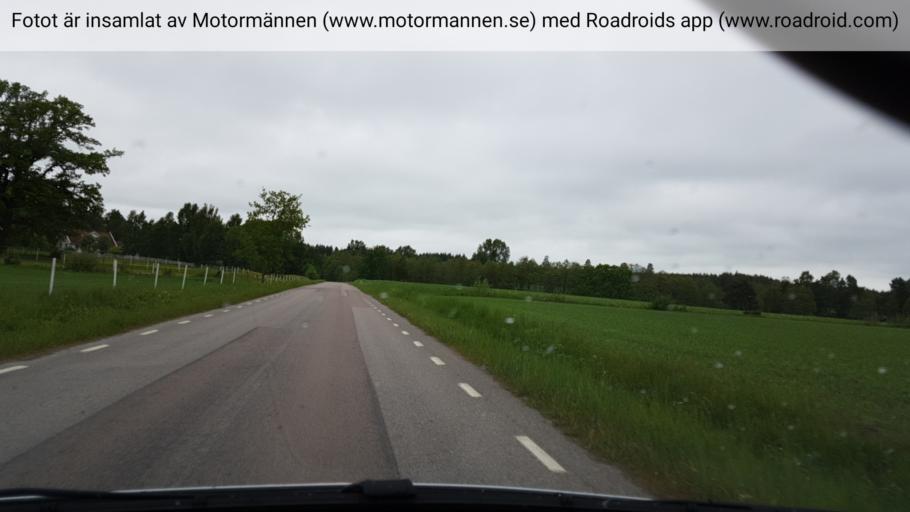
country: SE
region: Vaestra Goetaland
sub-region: Lidkopings Kommun
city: Vinninga
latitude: 58.4256
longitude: 13.3501
